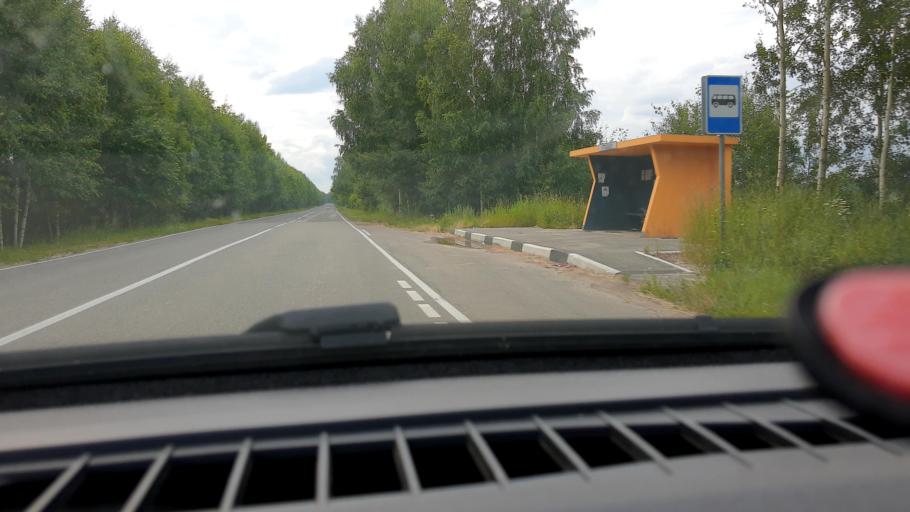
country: RU
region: Nizjnij Novgorod
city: Neklyudovo
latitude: 56.5131
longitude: 43.9430
